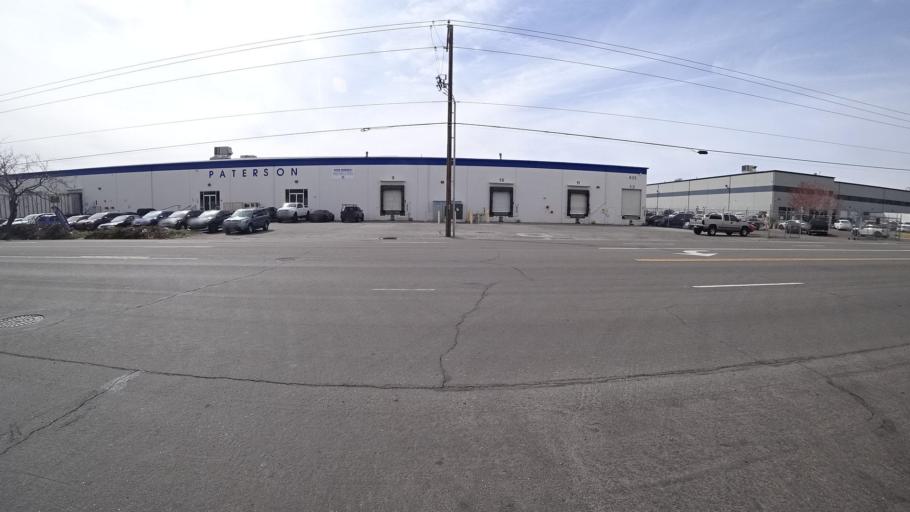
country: US
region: Nevada
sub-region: Washoe County
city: Sparks
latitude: 39.5216
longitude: -119.7512
